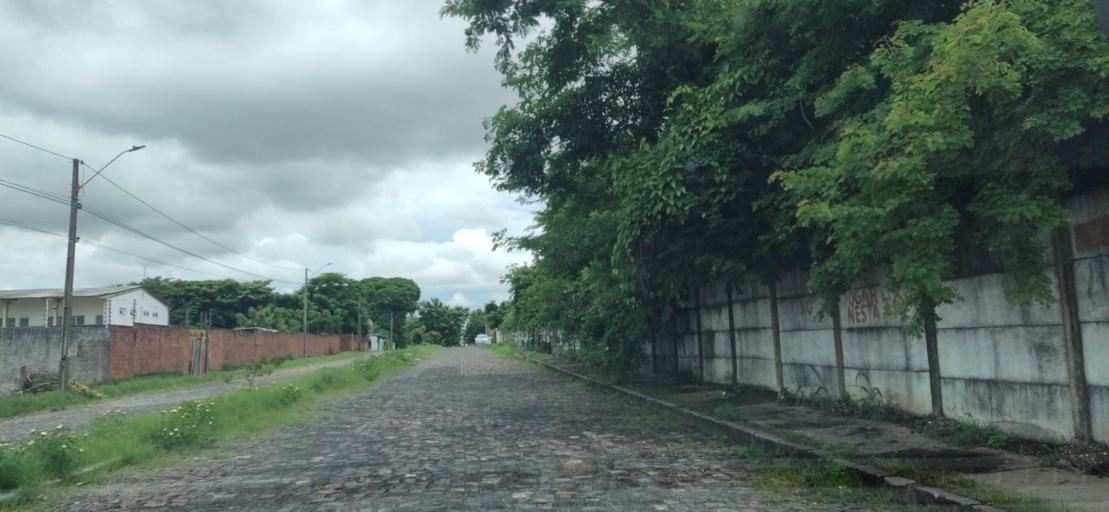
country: BR
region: Piaui
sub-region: Teresina
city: Teresina
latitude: -5.0749
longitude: -42.7603
